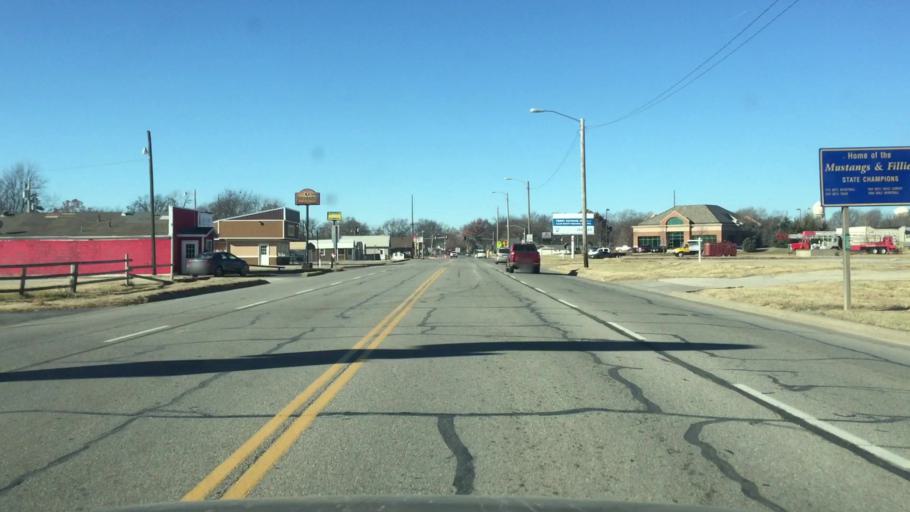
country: US
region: Kansas
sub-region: Allen County
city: Iola
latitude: 37.9222
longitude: -95.3877
